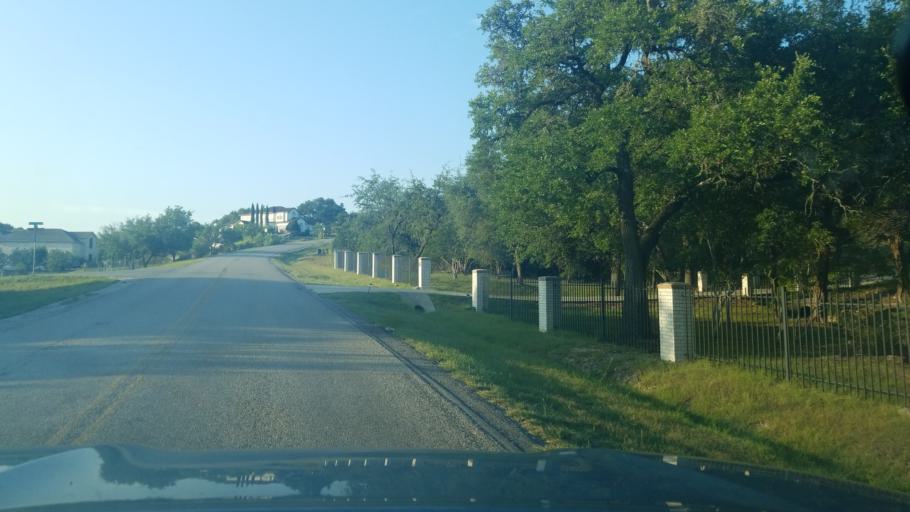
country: US
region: Texas
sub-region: Comal County
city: Bulverde
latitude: 29.8116
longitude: -98.4075
